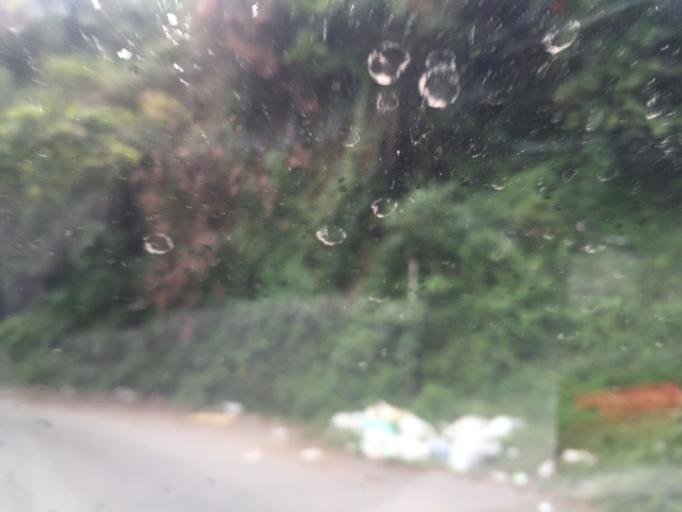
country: CO
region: Tolima
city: Cajamarca
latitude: 4.4255
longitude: -75.4323
